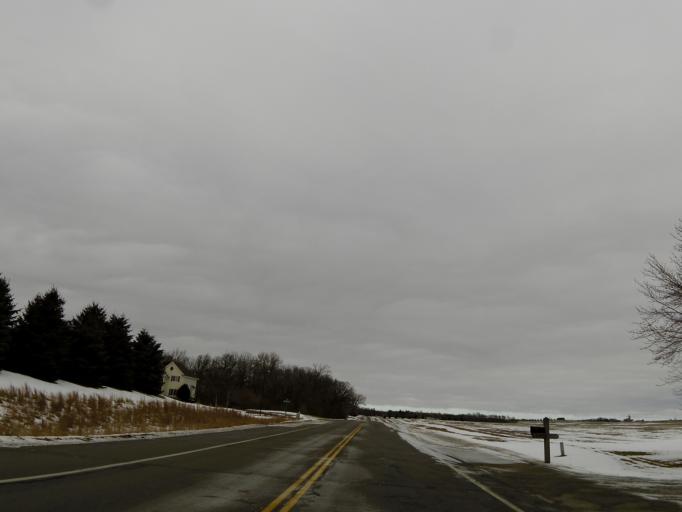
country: US
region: Minnesota
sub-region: Washington County
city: Cottage Grove
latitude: 44.7987
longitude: -92.8930
